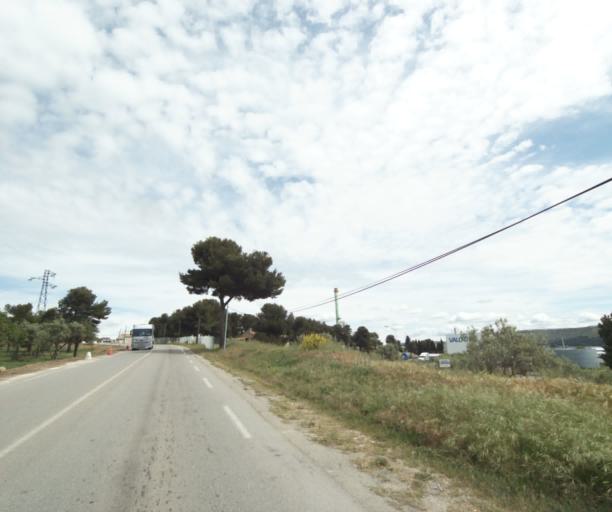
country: FR
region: Provence-Alpes-Cote d'Azur
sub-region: Departement des Bouches-du-Rhone
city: Rognac
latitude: 43.4946
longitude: 5.2054
